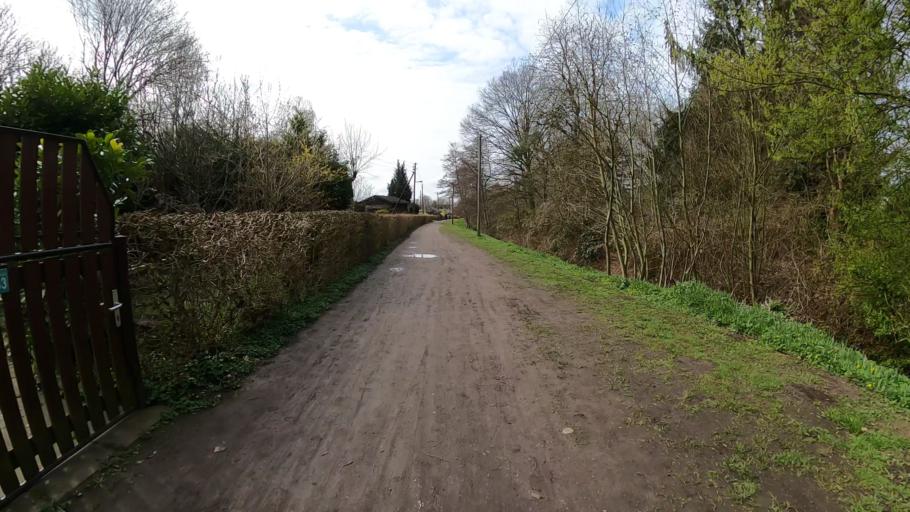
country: DE
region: Hamburg
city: Steilshoop
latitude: 53.5975
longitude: 10.0769
